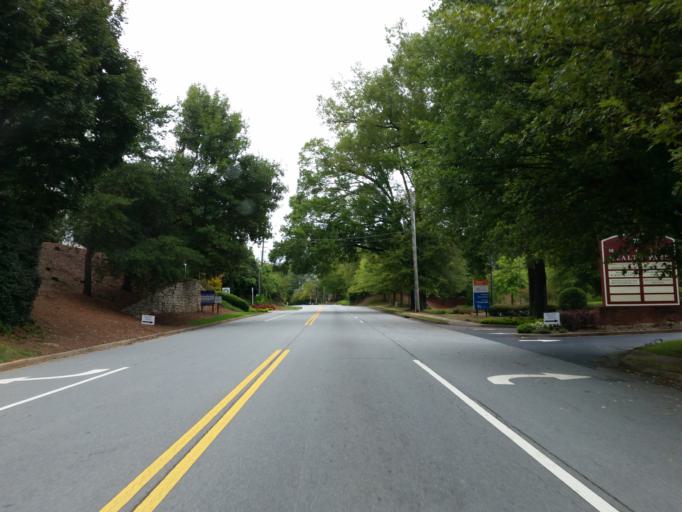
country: US
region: Georgia
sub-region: Cobb County
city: Marietta
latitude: 33.9706
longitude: -84.5479
